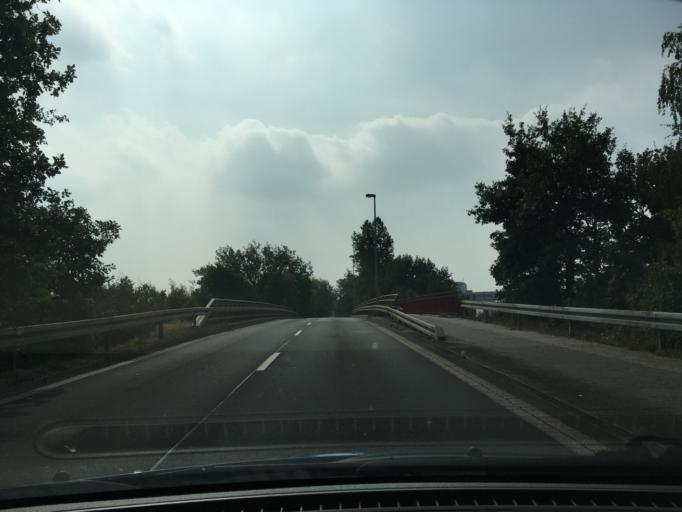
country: DE
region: Lower Saxony
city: Langenhagen
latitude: 52.4461
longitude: 9.7110
